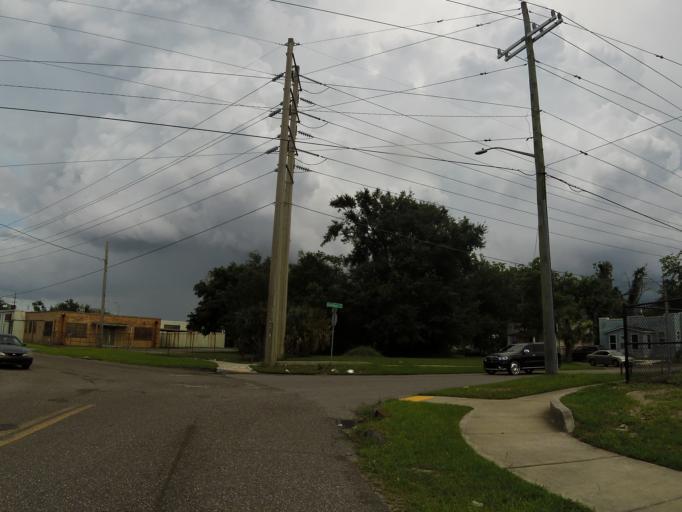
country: US
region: Florida
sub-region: Duval County
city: Jacksonville
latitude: 30.3706
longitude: -81.6612
